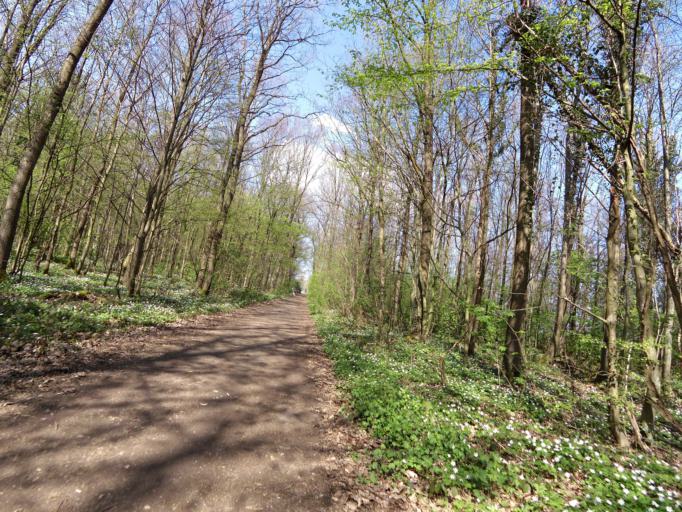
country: DE
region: North Rhine-Westphalia
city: Meckenheim
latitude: 50.6699
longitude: 7.0130
